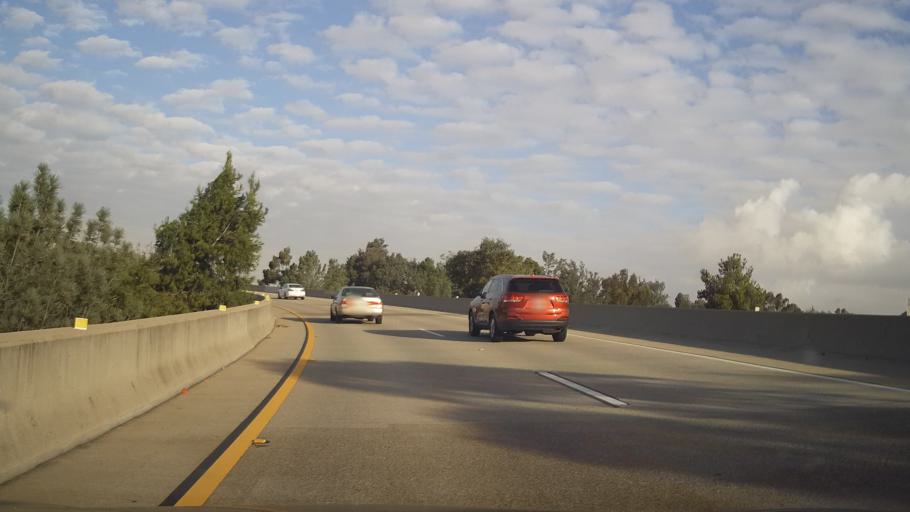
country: US
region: California
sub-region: San Diego County
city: La Mesa
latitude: 32.8219
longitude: -117.1135
